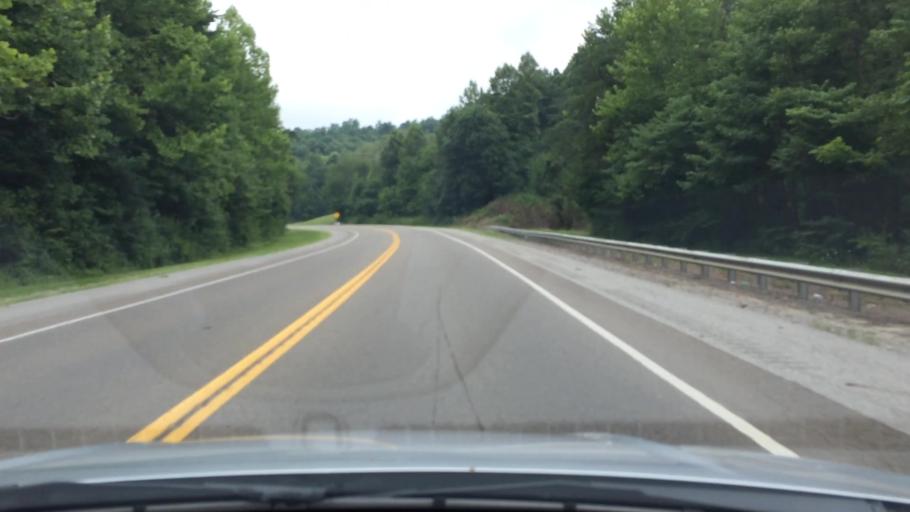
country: US
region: Tennessee
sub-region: Scott County
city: Huntsville
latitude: 36.4059
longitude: -84.4519
